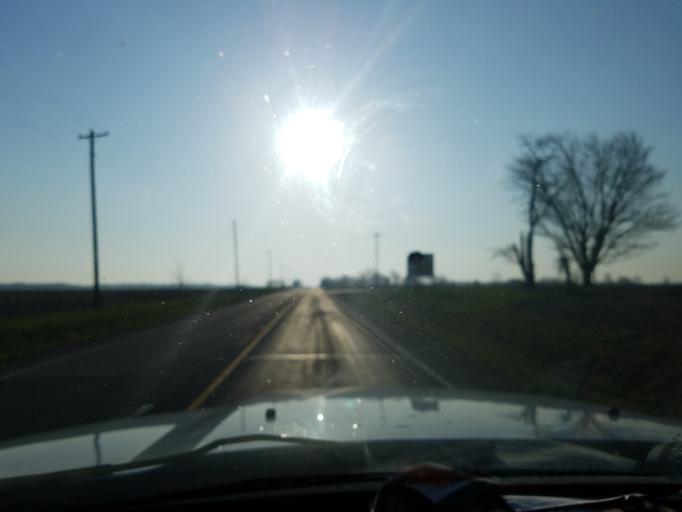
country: US
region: Indiana
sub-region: Vigo County
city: Seelyville
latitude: 39.3892
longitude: -87.2079
